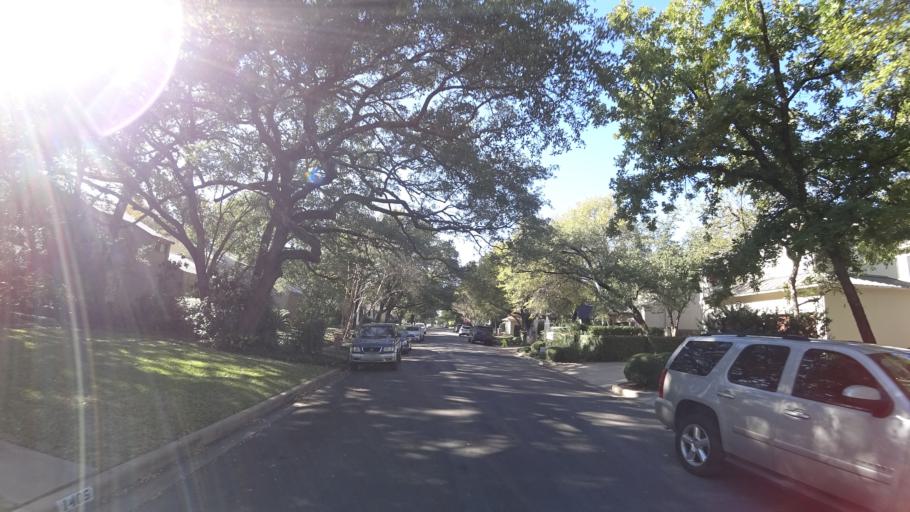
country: US
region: Texas
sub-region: Travis County
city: Austin
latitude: 30.2992
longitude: -97.7518
